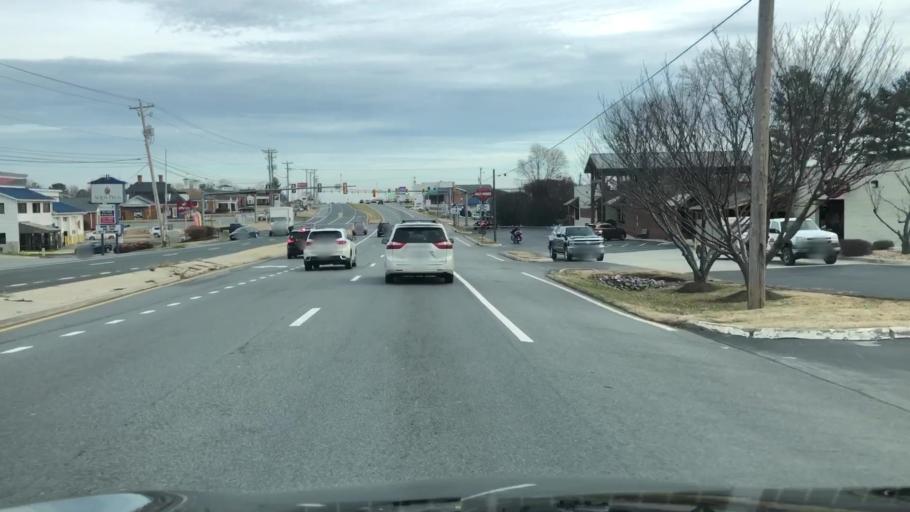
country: US
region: Virginia
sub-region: Campbell County
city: Timberlake
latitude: 37.3411
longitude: -79.2369
